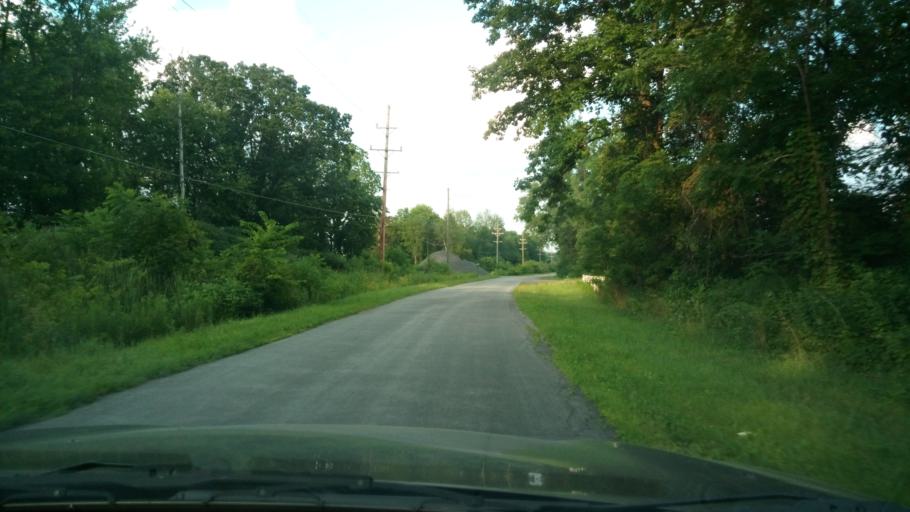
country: US
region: New York
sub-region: Wayne County
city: Clyde
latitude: 43.0878
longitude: -76.9098
